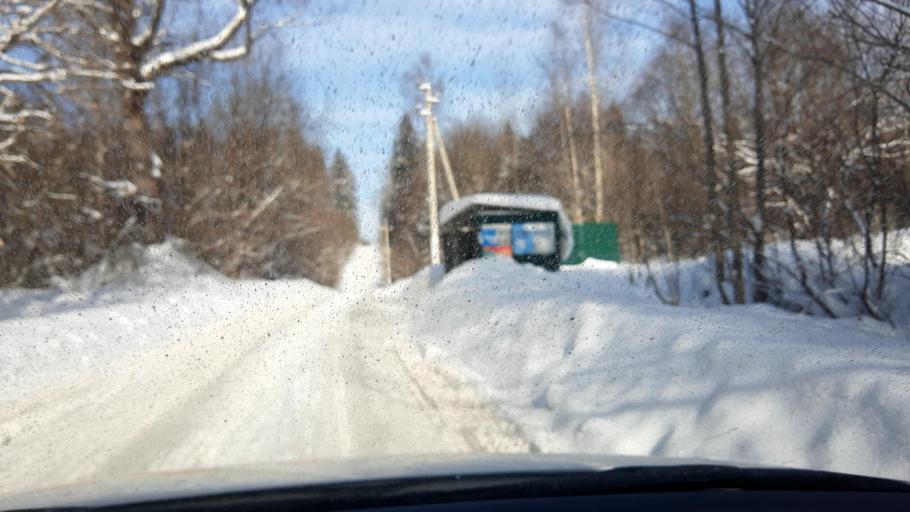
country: RU
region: Moskovskaya
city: Rumyantsevo
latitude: 55.9087
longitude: 36.5815
